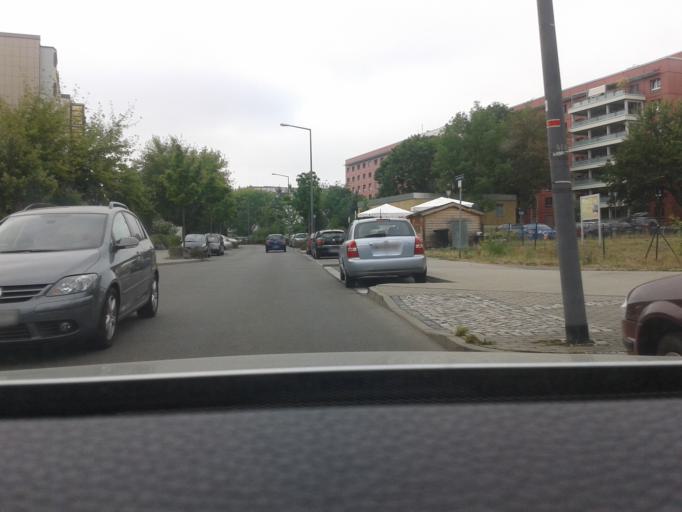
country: DE
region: Saxony
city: Dresden
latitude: 51.0063
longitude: 13.7935
